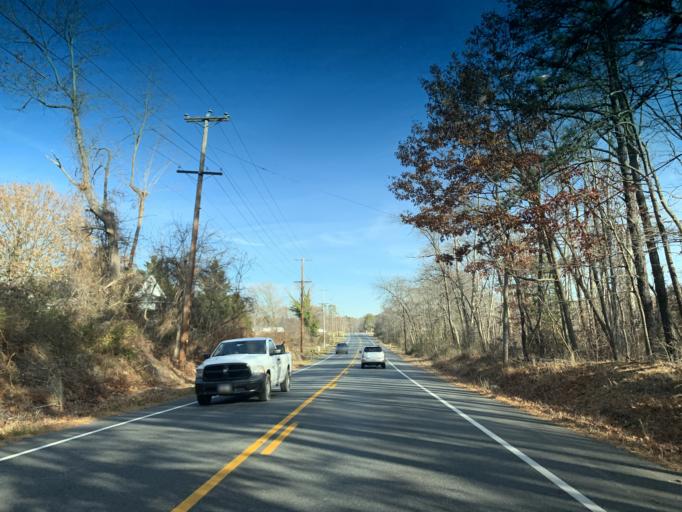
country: US
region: Maryland
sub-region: Cecil County
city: North East
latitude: 39.6040
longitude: -75.8954
